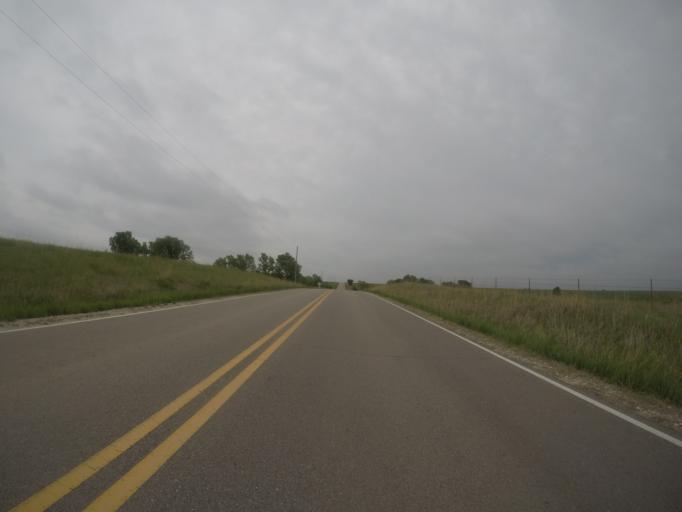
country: US
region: Kansas
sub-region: Pottawatomie County
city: Westmoreland
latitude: 39.5115
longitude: -96.2373
